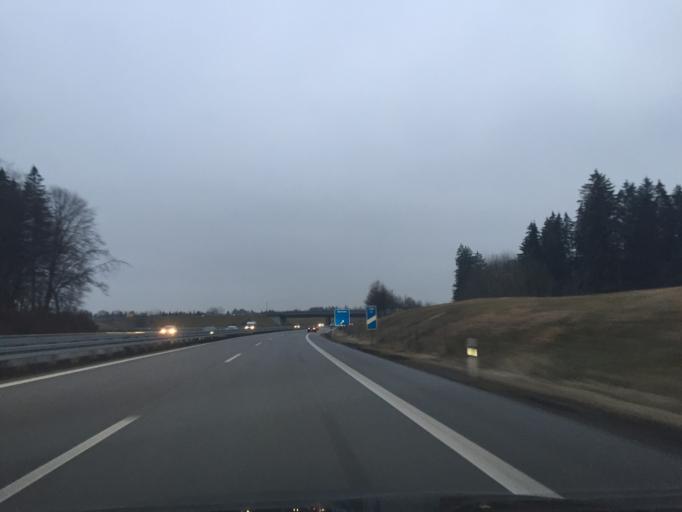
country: DE
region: Bavaria
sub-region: Upper Bavaria
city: Wessling
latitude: 48.0884
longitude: 11.2297
